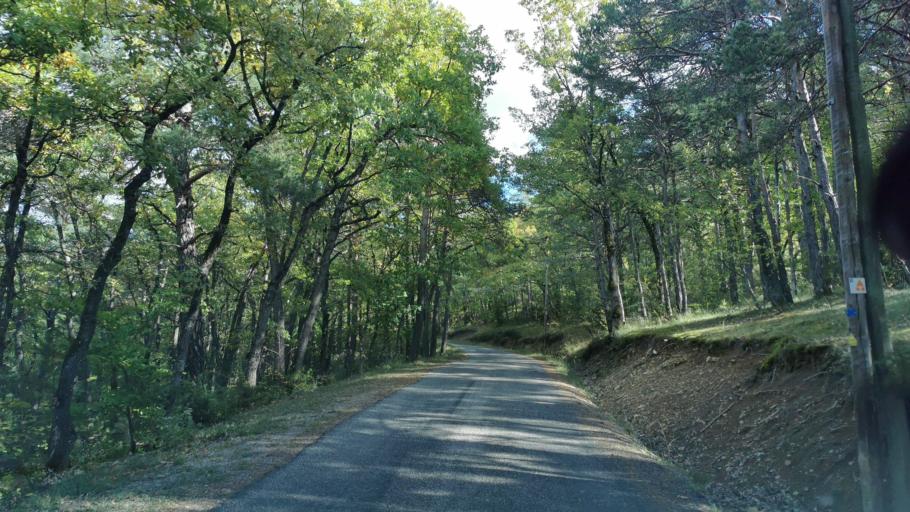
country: FR
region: Provence-Alpes-Cote d'Azur
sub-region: Departement des Alpes-de-Haute-Provence
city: Volonne
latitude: 44.1823
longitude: 6.0304
